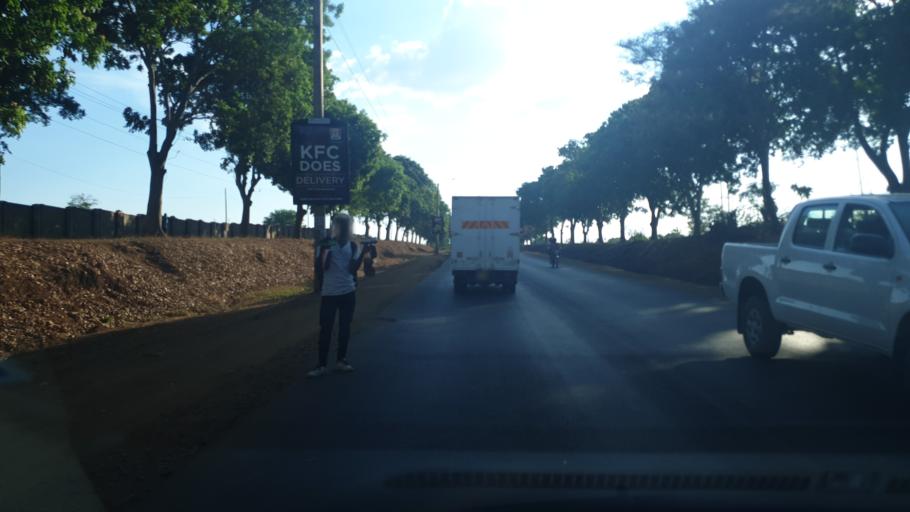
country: MW
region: Central Region
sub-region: Lilongwe District
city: Lilongwe
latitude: -13.9724
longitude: 33.7825
